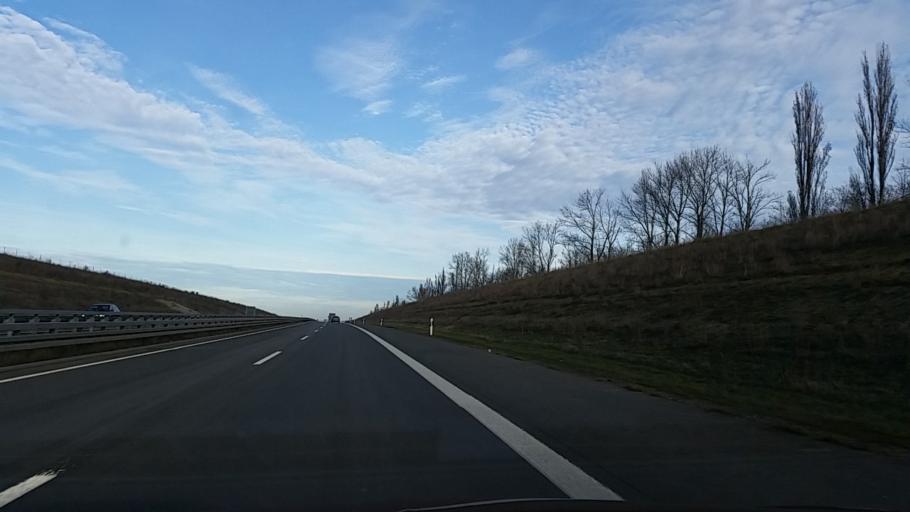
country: DE
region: Thuringia
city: Schillingstedt
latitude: 51.2132
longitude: 11.1854
